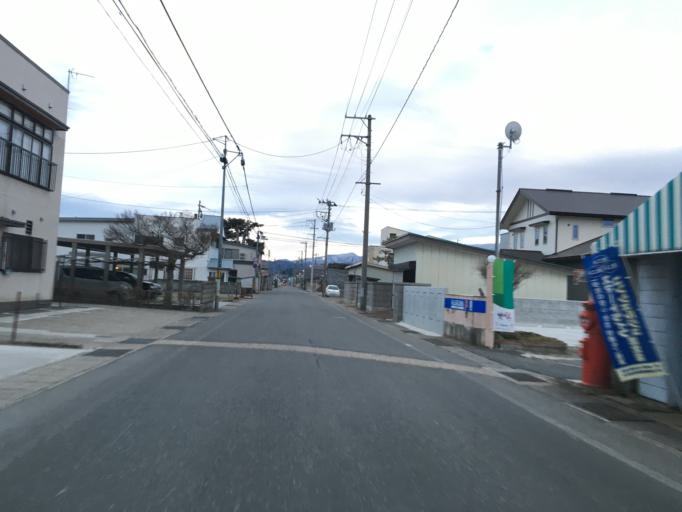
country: JP
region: Yamagata
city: Yonezawa
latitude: 37.9188
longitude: 140.0939
